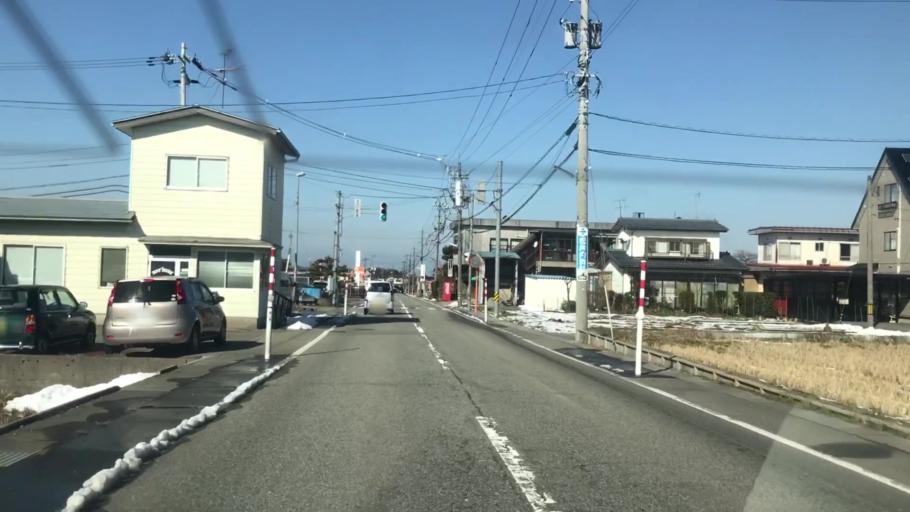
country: JP
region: Toyama
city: Toyama-shi
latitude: 36.6502
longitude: 137.2461
